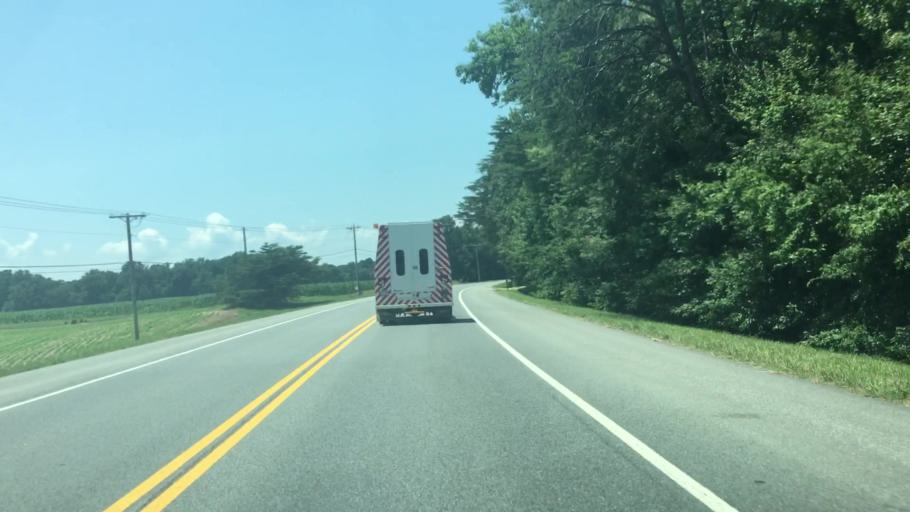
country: US
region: Maryland
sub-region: Saint Mary's County
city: Mechanicsville
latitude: 38.3720
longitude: -76.8000
